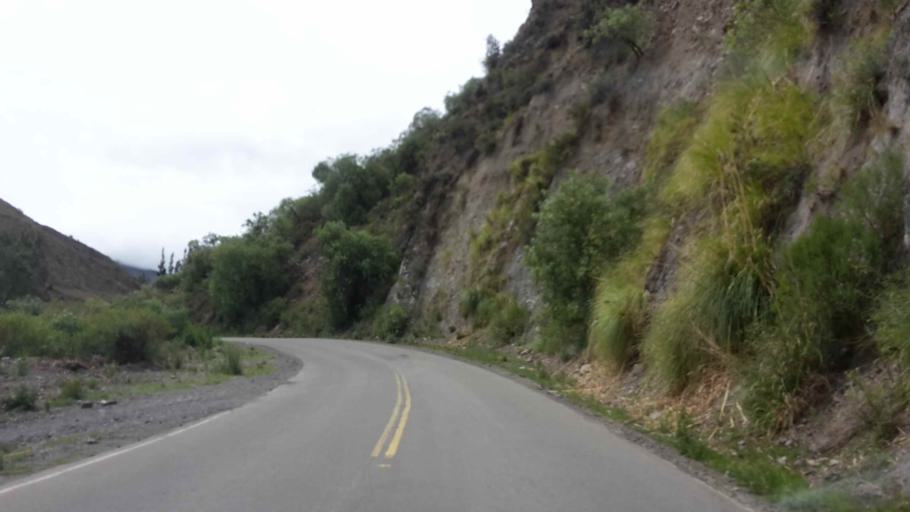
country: BO
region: Cochabamba
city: Colomi
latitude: -17.4088
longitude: -65.7860
